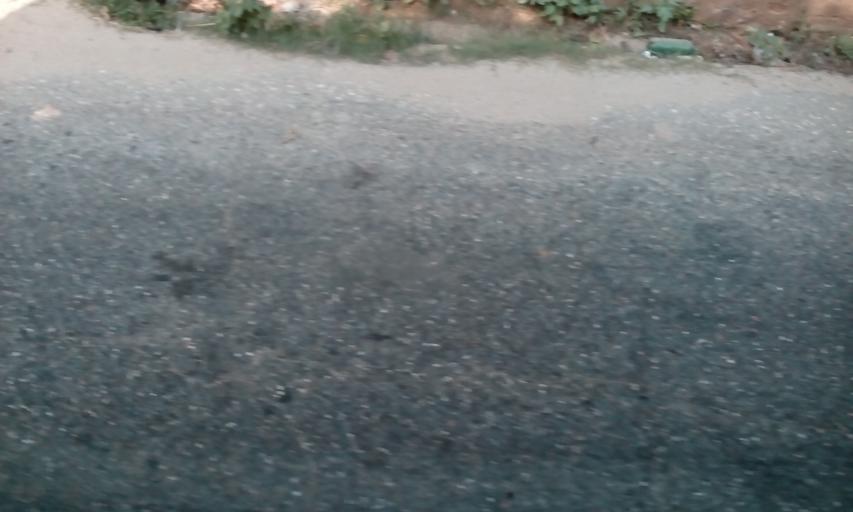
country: NP
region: Central Region
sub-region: Narayani Zone
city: Bharatpur
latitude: 27.8094
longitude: 84.8340
